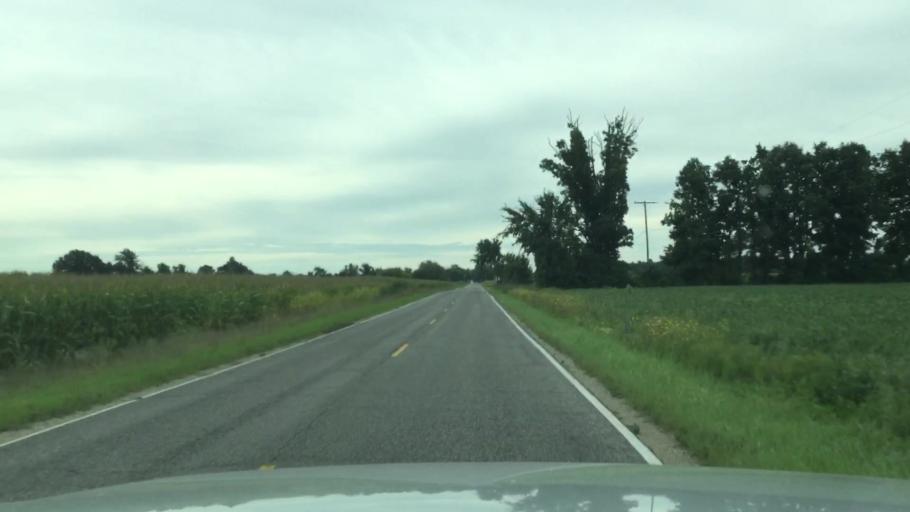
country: US
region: Michigan
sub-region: Genesee County
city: Flushing
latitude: 43.0669
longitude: -83.9876
